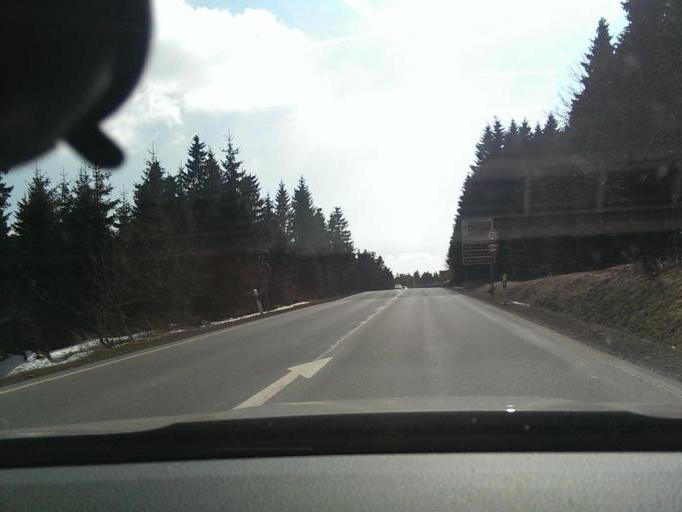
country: DE
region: Thuringia
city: Oberhof
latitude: 50.6980
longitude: 10.7224
